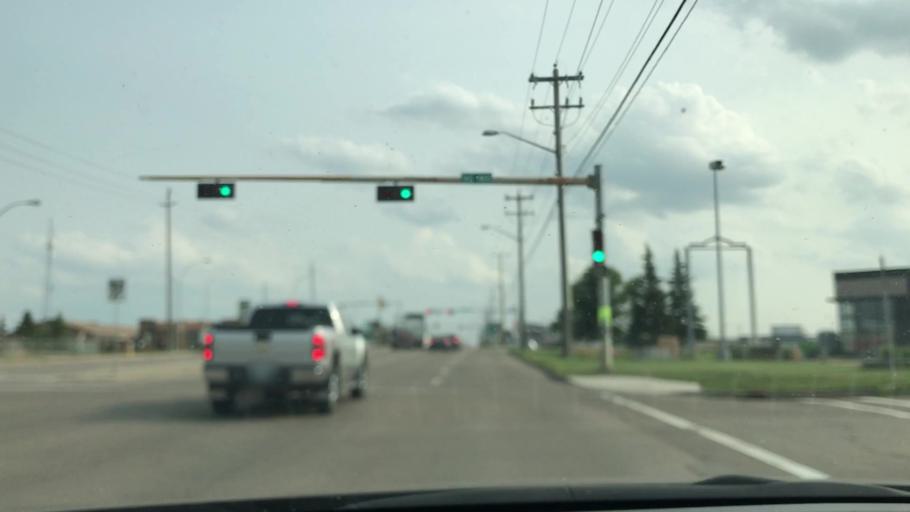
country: CA
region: Alberta
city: Edmonton
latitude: 53.5161
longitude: -113.4187
